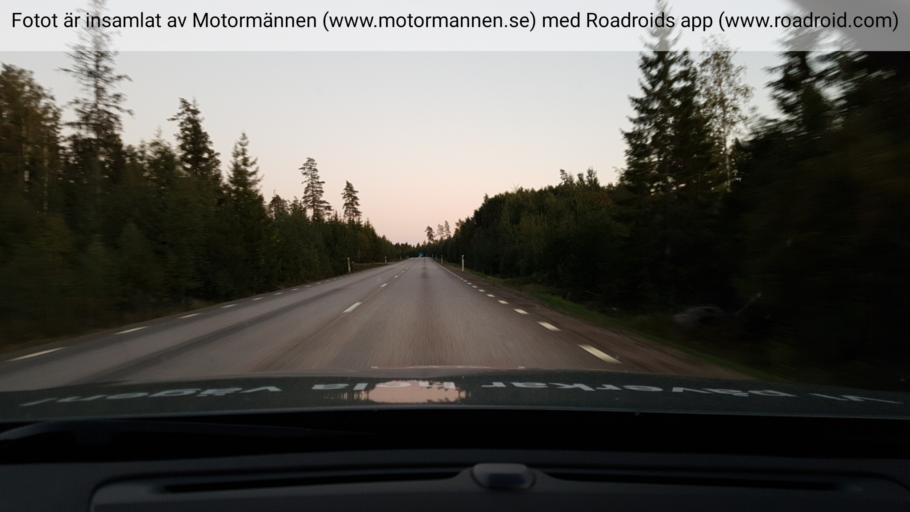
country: SE
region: OErebro
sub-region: Laxa Kommun
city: Laxa
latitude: 58.9478
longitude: 14.6287
